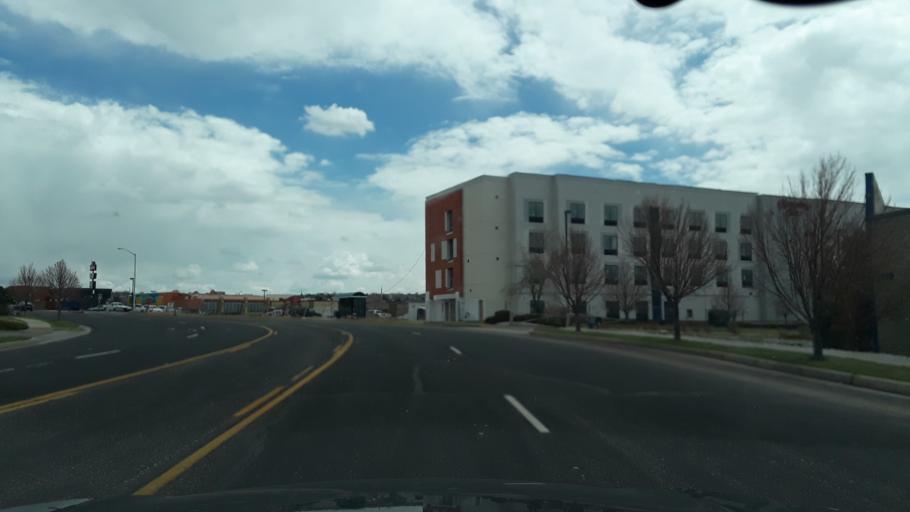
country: US
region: Colorado
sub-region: El Paso County
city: Air Force Academy
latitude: 38.9476
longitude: -104.8060
